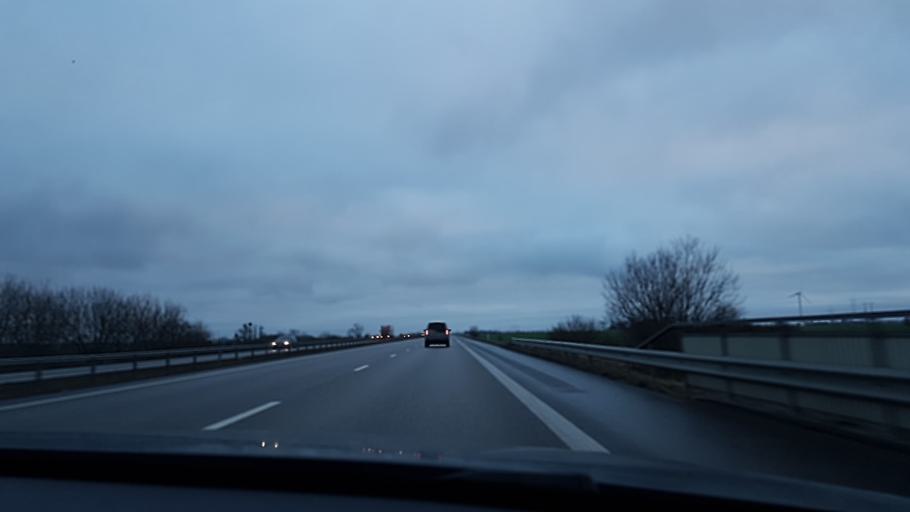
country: SE
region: Skane
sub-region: Astorps Kommun
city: Astorp
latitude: 56.1729
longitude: 12.9926
